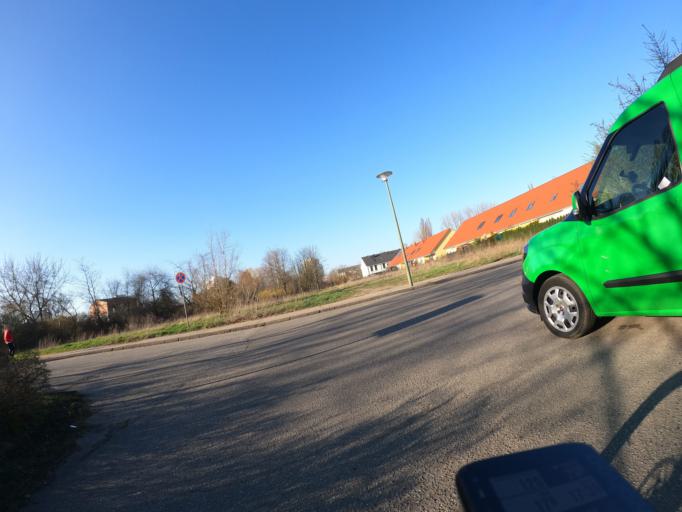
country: DE
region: Berlin
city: Marzahn
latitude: 52.5413
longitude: 13.5582
